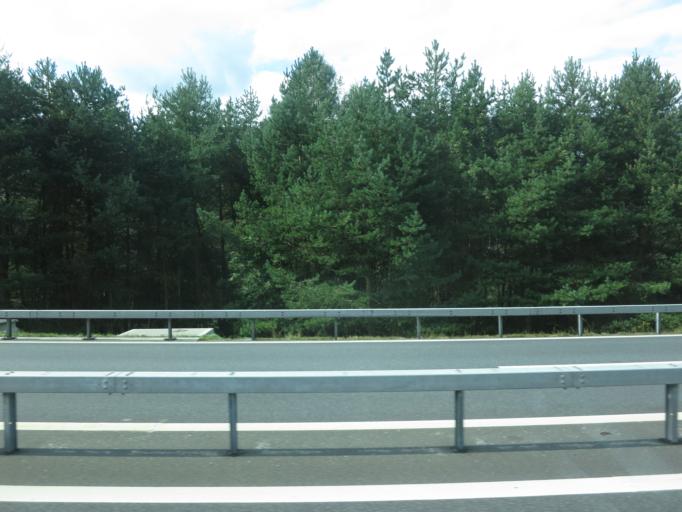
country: CH
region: Grisons
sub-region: Hinterrhein District
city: Cazis
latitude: 46.7281
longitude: 9.4405
